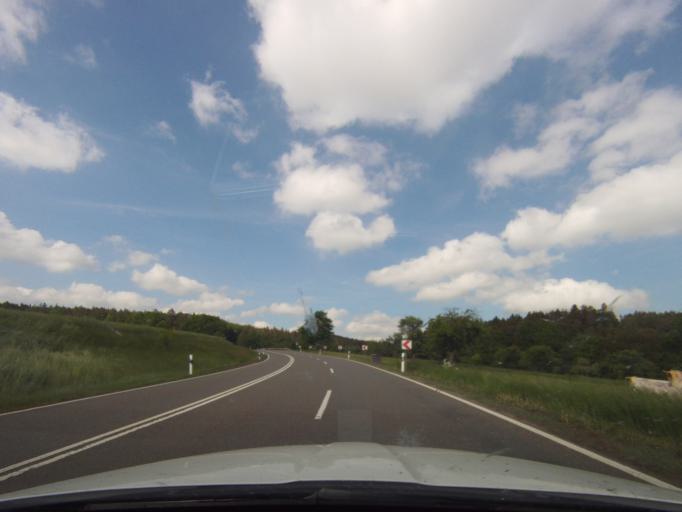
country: DE
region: Thuringia
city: Renthendorf
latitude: 50.7886
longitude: 11.9695
